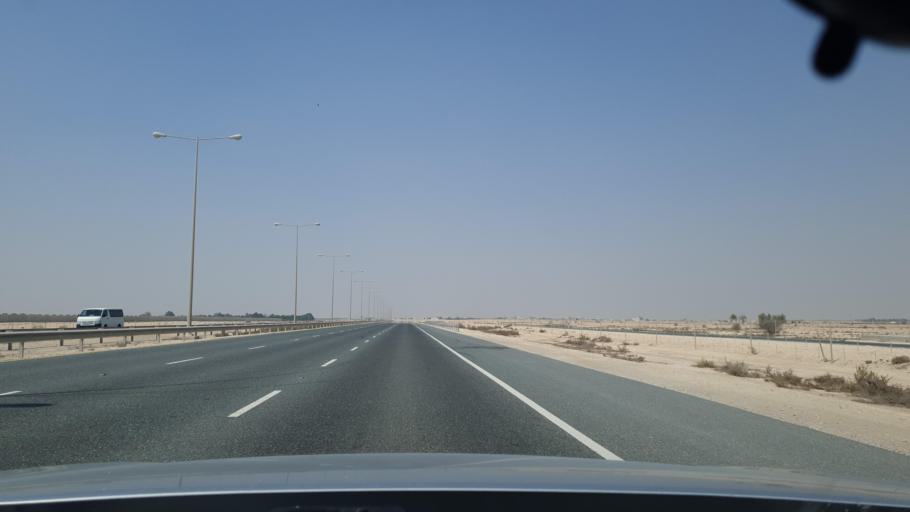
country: QA
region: Al Khawr
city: Al Khawr
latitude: 25.7690
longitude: 51.4159
